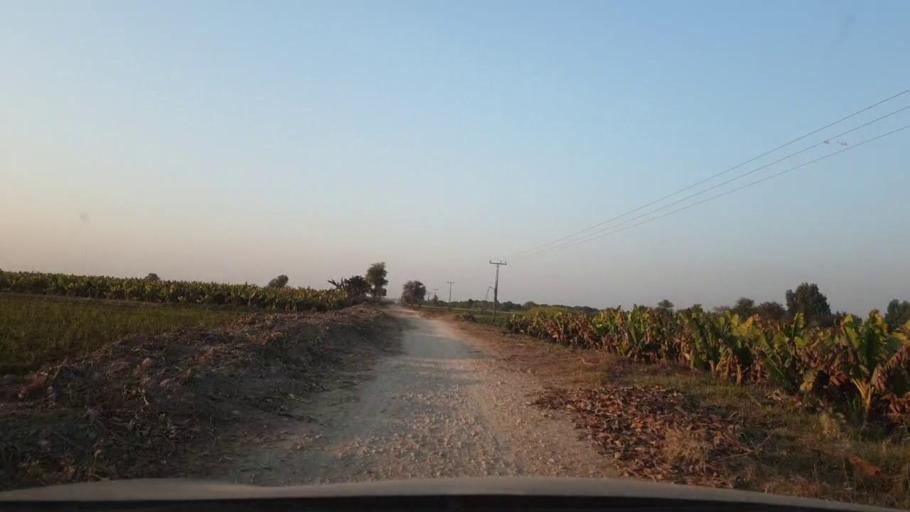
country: PK
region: Sindh
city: Tando Allahyar
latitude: 25.5144
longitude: 68.7393
